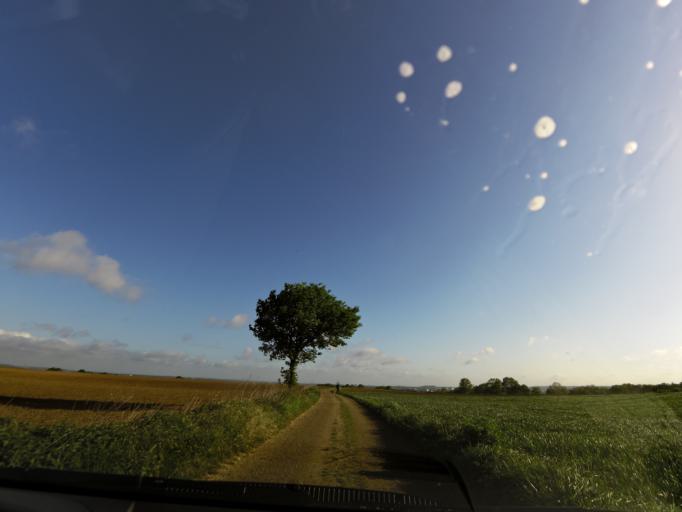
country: NL
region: Limburg
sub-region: Gemeente Voerendaal
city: Ubachsberg
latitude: 50.8627
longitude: 5.9551
